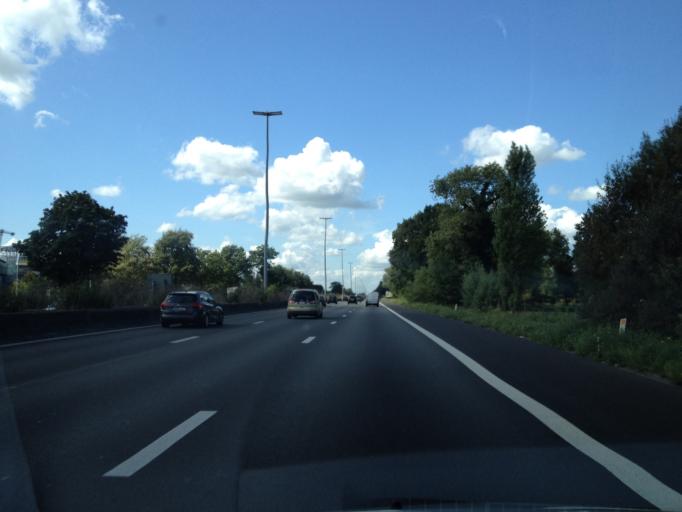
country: BE
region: Flanders
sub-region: Provincie Oost-Vlaanderen
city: Sint-Martens-Latem
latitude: 51.0420
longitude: 3.6091
